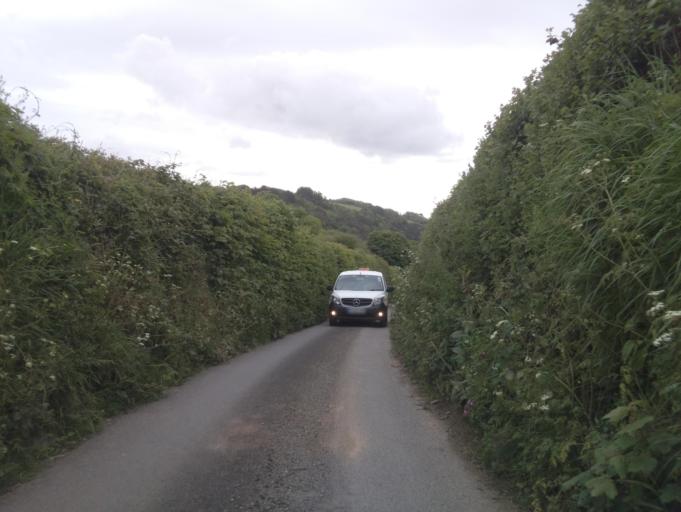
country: GB
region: England
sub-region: Devon
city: Dartmouth
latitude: 50.3196
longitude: -3.6201
